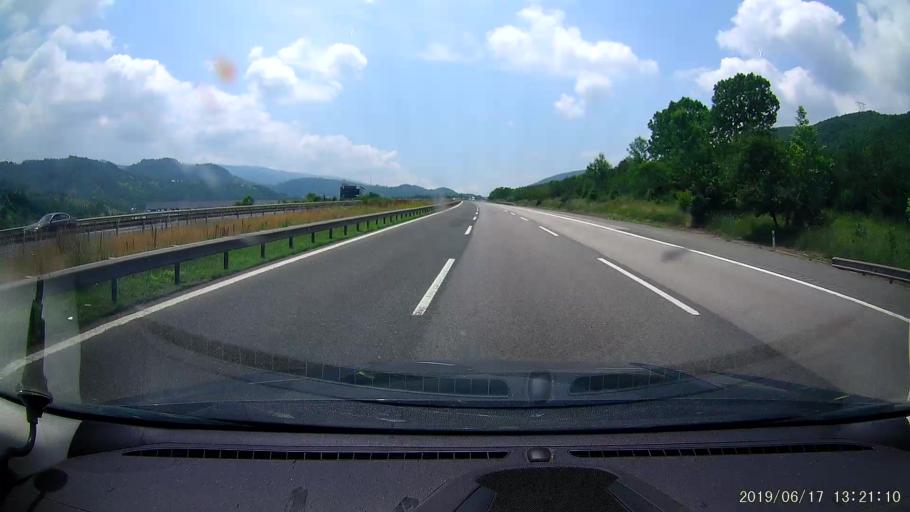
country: TR
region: Duzce
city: Gumusova
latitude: 40.8363
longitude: 30.9425
